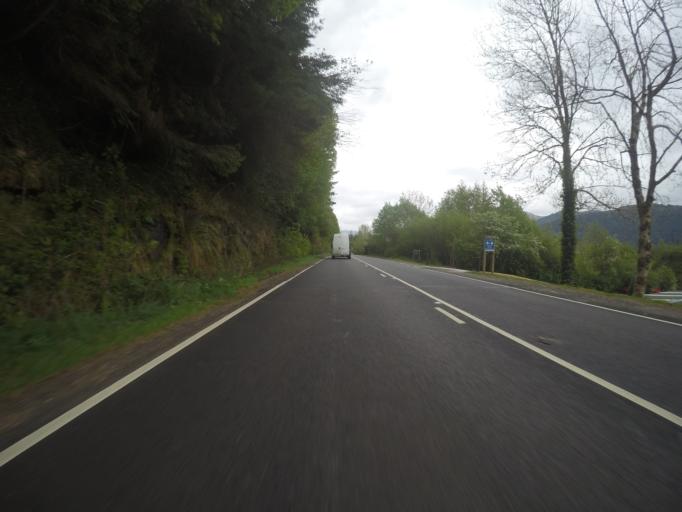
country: GB
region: Scotland
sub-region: Highland
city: Fort William
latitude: 57.2459
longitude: -5.4635
